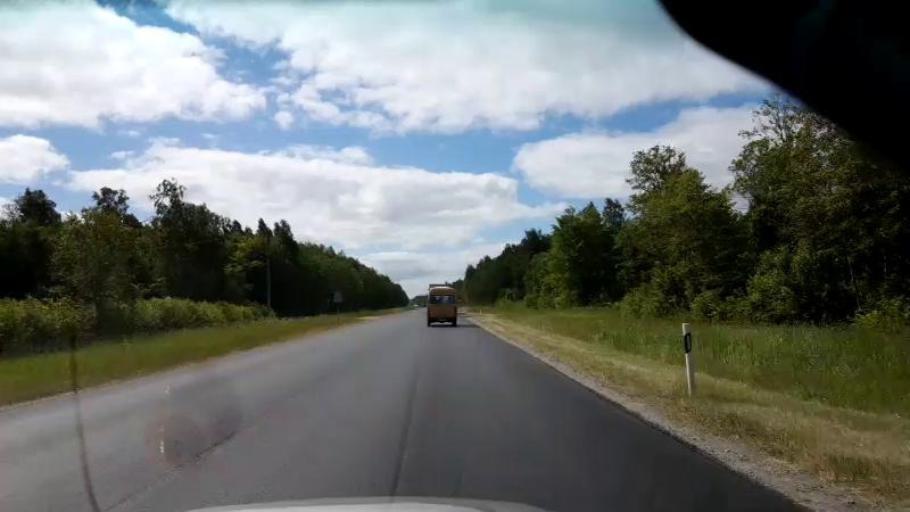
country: LV
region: Salacgrivas
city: Ainazi
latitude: 57.9377
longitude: 24.4298
